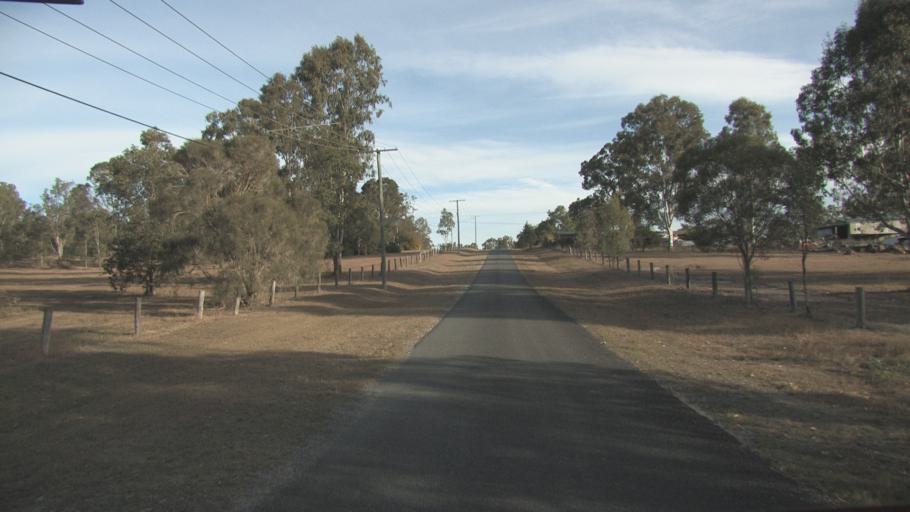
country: AU
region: Queensland
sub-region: Logan
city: Cedar Vale
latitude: -27.8550
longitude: 153.0613
